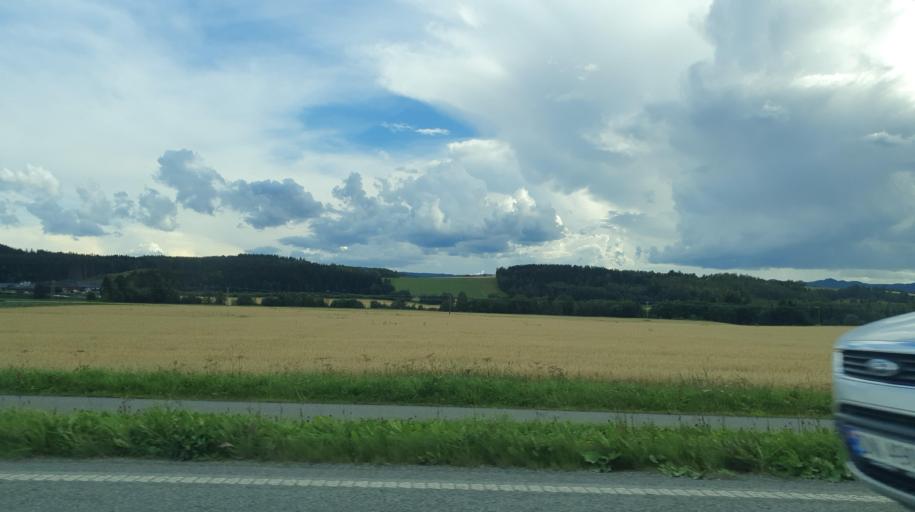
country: NO
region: Nord-Trondelag
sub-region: Levanger
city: Levanger
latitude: 63.7535
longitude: 11.3643
